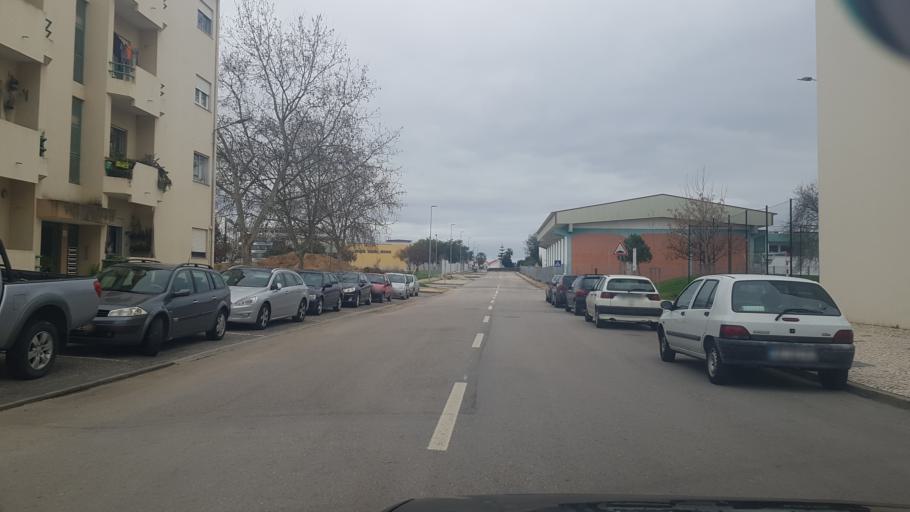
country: PT
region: Santarem
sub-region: Entroncamento
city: Entroncamento
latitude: 39.4564
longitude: -8.4674
